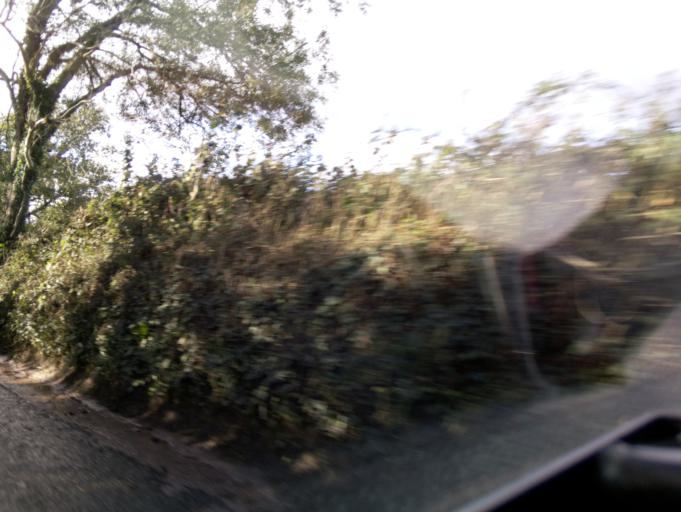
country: GB
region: England
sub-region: Devon
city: Totnes
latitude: 50.3594
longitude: -3.7316
